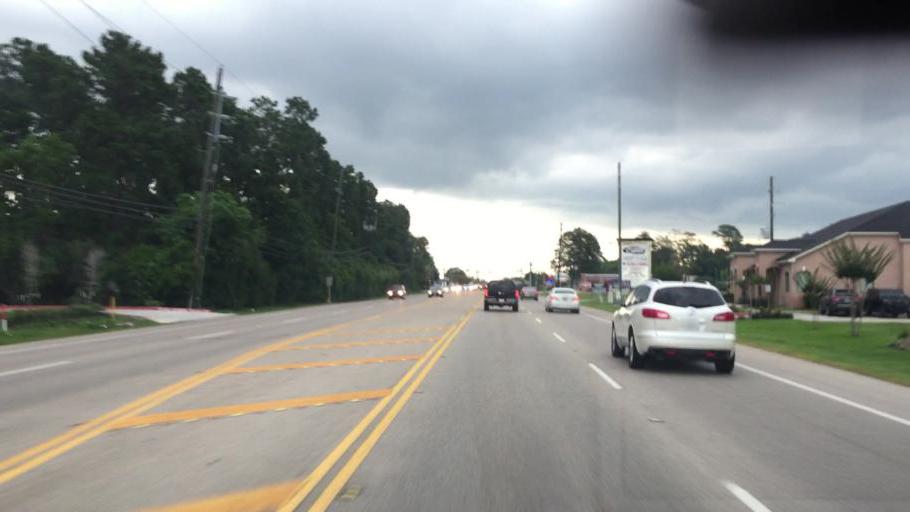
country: US
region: Texas
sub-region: Harris County
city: Spring
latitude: 30.0349
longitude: -95.4985
